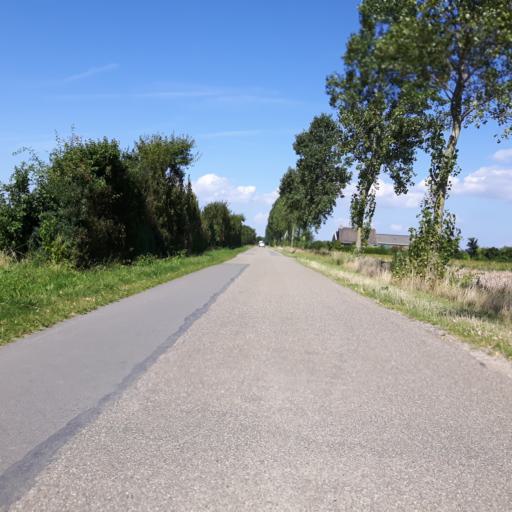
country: NL
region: Zeeland
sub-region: Schouwen-Duiveland
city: Bruinisse
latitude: 51.6266
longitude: 3.9761
